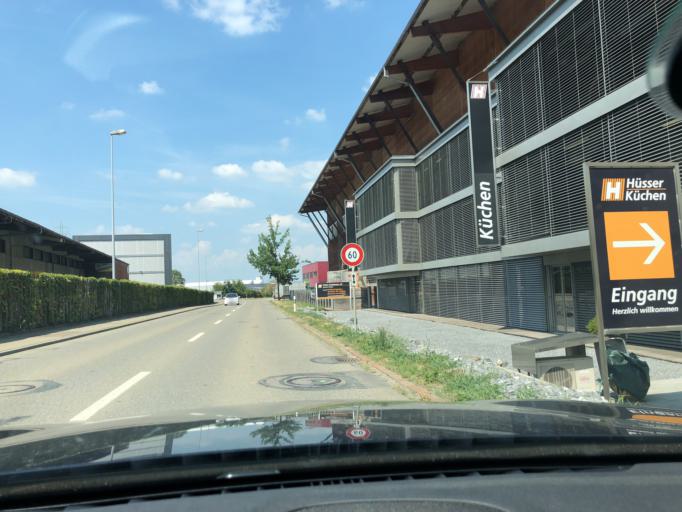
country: CH
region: Aargau
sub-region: Bezirk Bremgarten
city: Bremgarten
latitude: 47.3516
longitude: 8.3288
